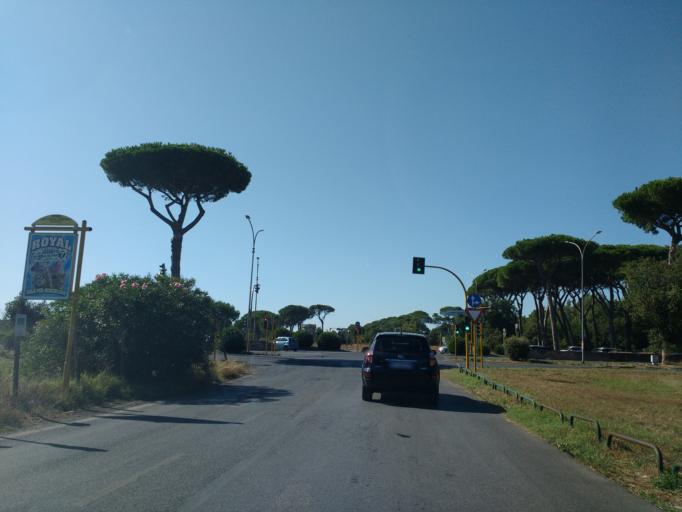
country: IT
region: Latium
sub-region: Citta metropolitana di Roma Capitale
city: Acilia-Castel Fusano-Ostia Antica
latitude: 41.7298
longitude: 12.3381
